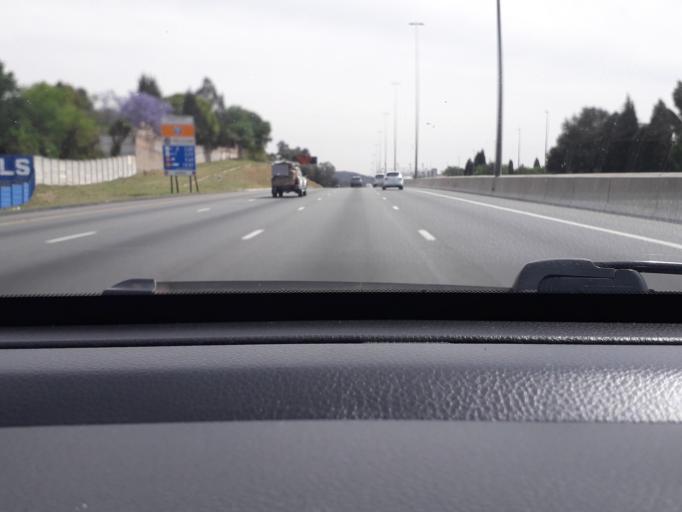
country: ZA
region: Gauteng
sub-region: City of Johannesburg Metropolitan Municipality
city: Diepsloot
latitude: -26.0577
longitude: 27.9881
